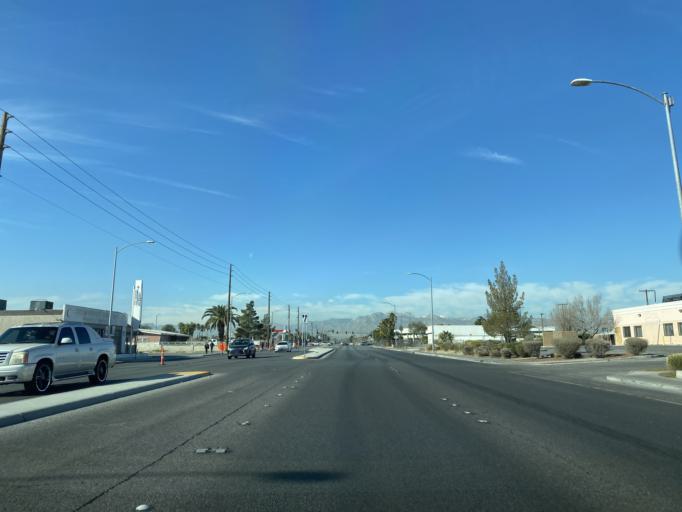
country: US
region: Nevada
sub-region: Clark County
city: Las Vegas
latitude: 36.1885
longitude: -115.1582
